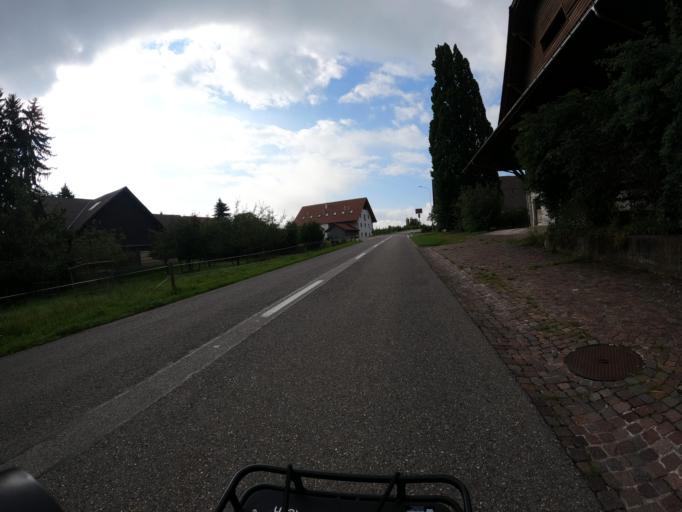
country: CH
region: Aargau
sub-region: Bezirk Muri
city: Buttwil
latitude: 47.2498
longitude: 8.3219
